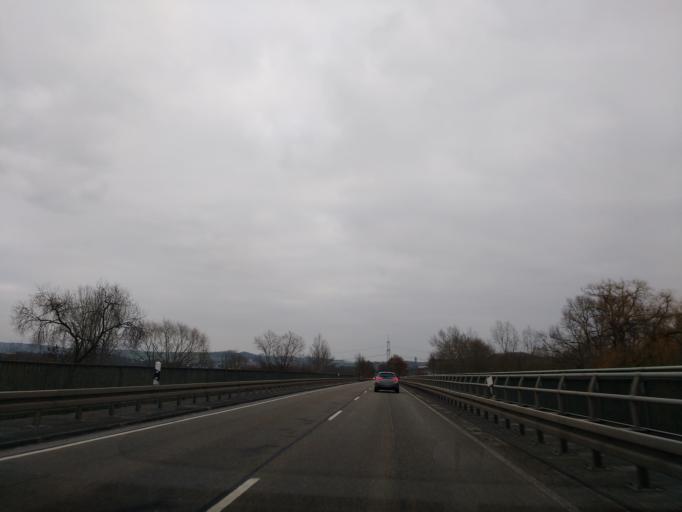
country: DE
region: Hesse
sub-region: Regierungsbezirk Kassel
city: Guxhagen
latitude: 51.2109
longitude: 9.4532
